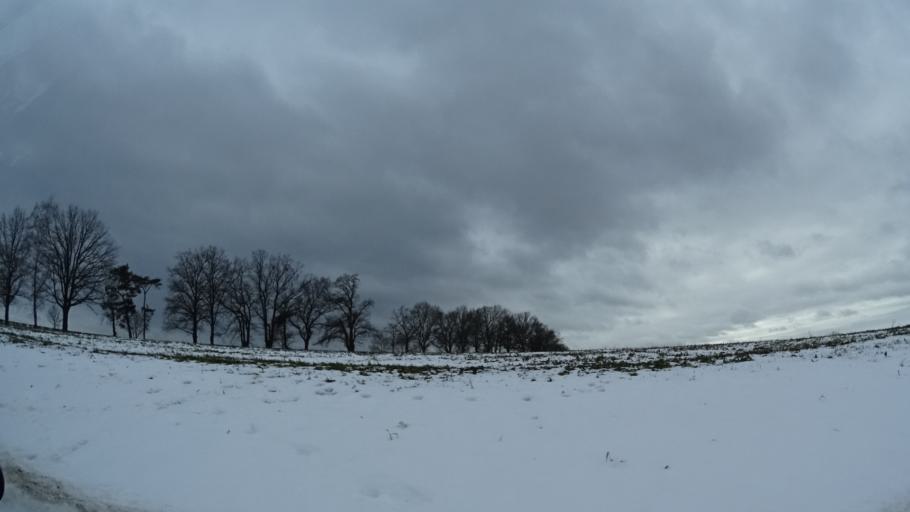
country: DE
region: Hesse
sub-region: Regierungsbezirk Darmstadt
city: Erbach
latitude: 49.6741
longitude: 8.9422
